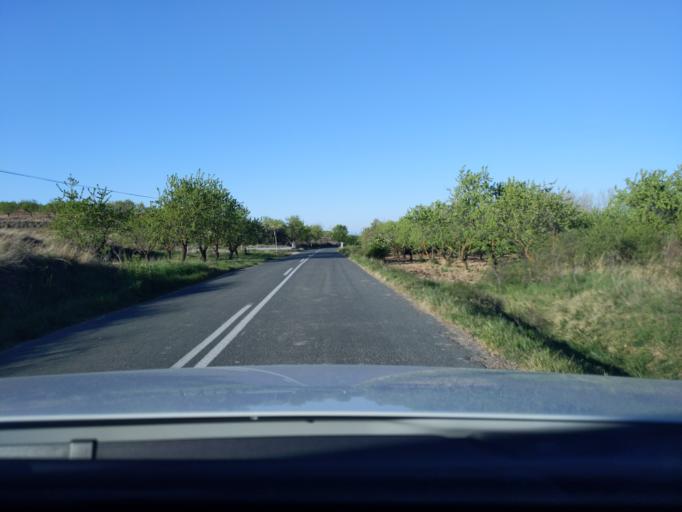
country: ES
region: La Rioja
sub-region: Provincia de La Rioja
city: Bergasa
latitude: 42.2625
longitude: -2.1088
